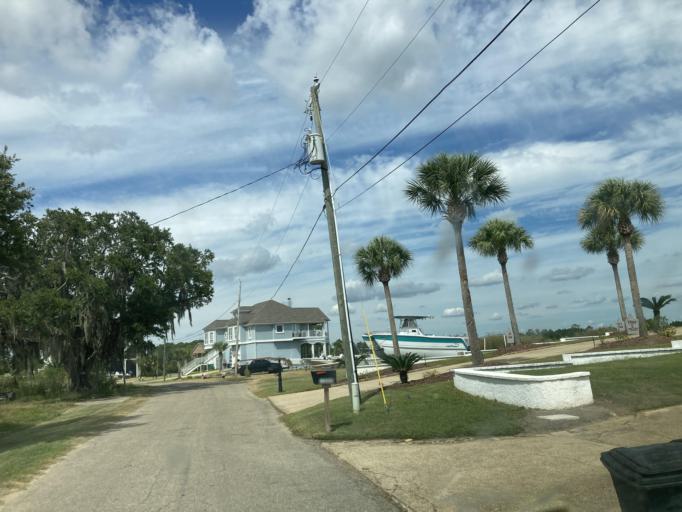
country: US
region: Mississippi
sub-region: Jackson County
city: Saint Martin
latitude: 30.4259
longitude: -88.8700
